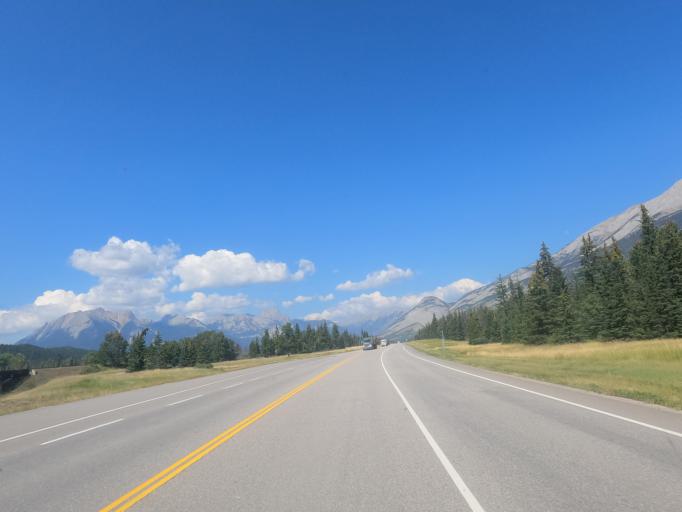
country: CA
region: Alberta
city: Jasper Park Lodge
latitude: 52.9705
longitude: -118.0569
